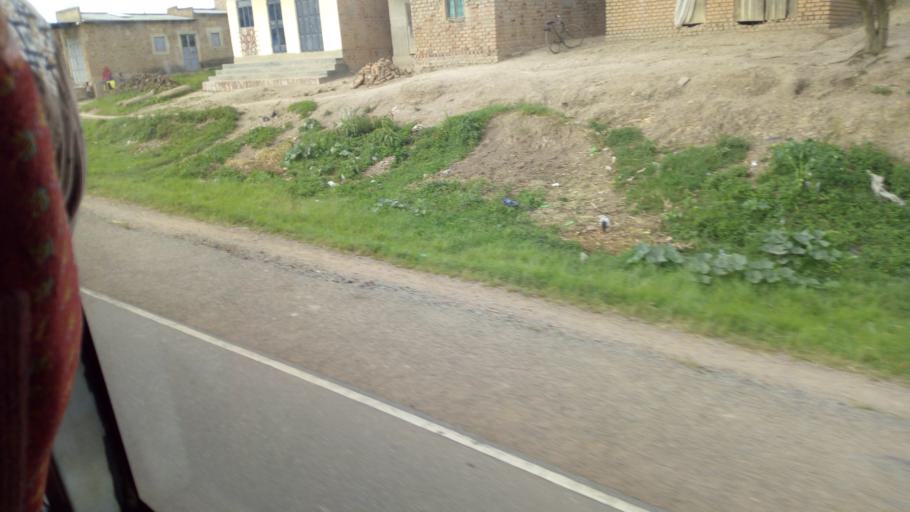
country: UG
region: Central Region
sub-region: Lyantonde District
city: Lyantonde
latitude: -0.3725
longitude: 31.2733
